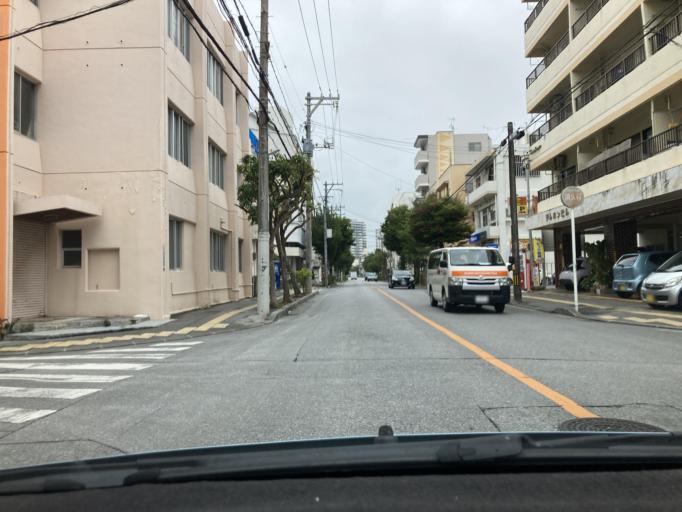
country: JP
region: Okinawa
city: Naha-shi
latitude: 26.2215
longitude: 127.6864
